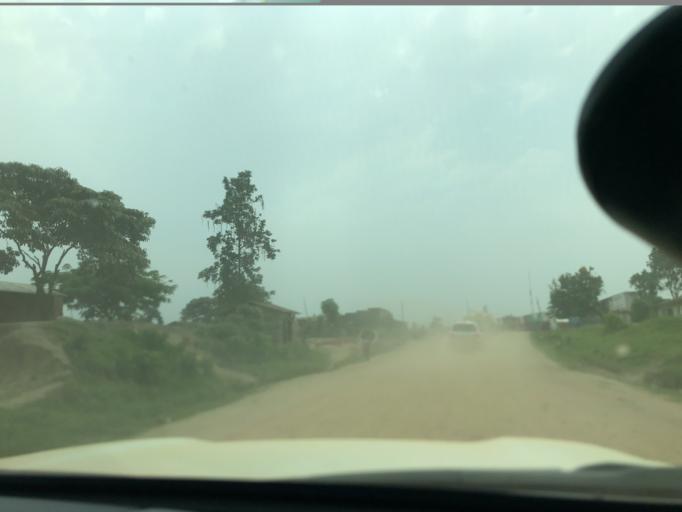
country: UG
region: Western Region
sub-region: Kasese District
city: Margherita
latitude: 0.3325
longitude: 29.6744
